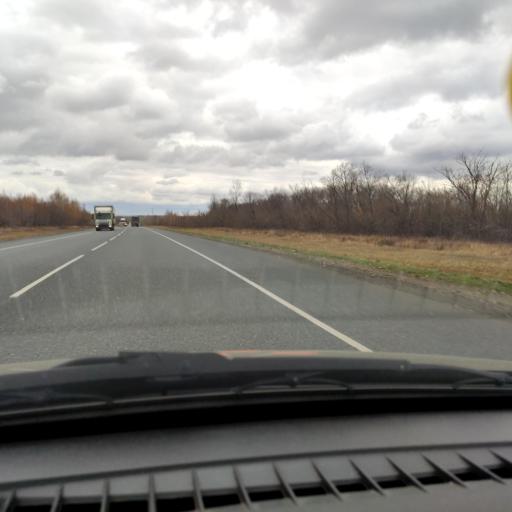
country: RU
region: Samara
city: Mezhdurechensk
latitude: 53.2385
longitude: 48.9599
